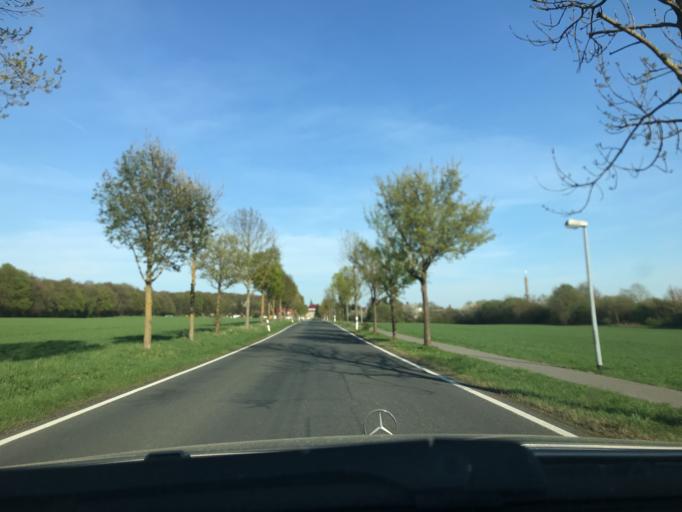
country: DE
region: Thuringia
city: Niederorschel
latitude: 51.3343
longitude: 10.4164
